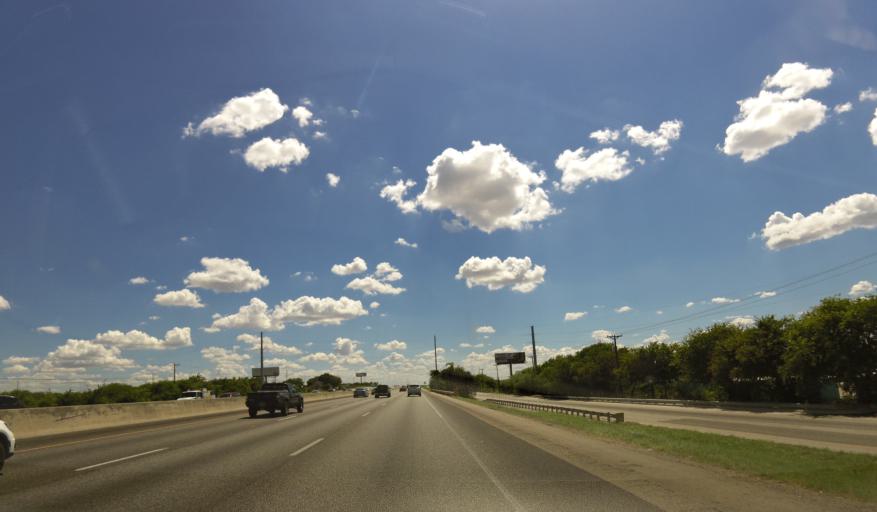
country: US
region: Texas
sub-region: Guadalupe County
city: Northcliff
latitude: 29.6479
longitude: -98.1986
